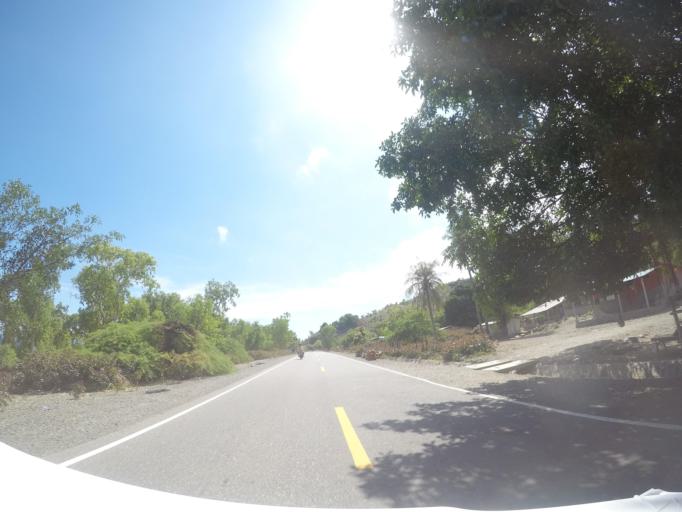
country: TL
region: Manatuto
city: Manatuto
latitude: -8.4771
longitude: 125.8805
